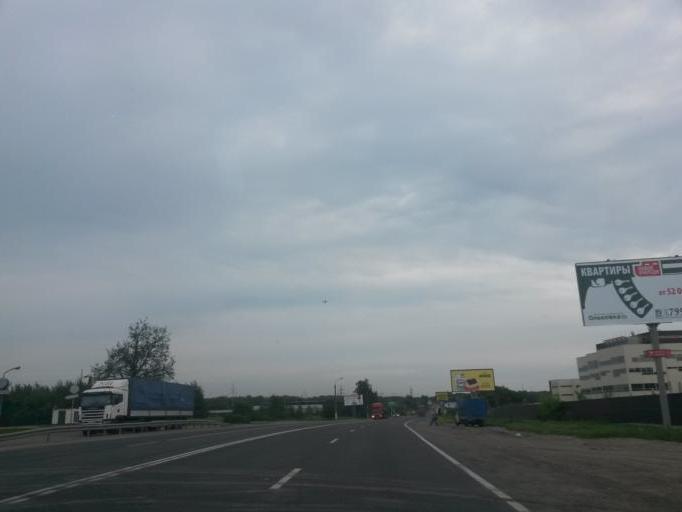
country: RU
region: Moskovskaya
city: Petrovskaya
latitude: 55.5464
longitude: 37.7739
